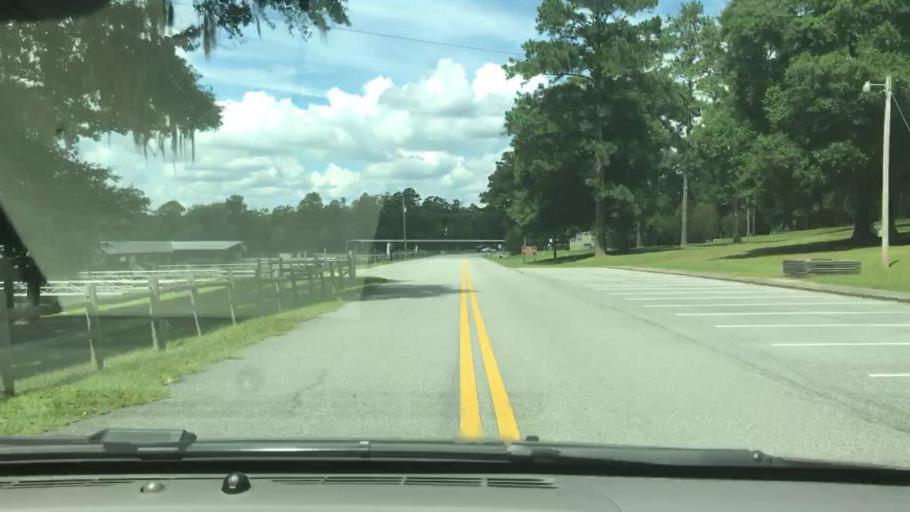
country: US
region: Georgia
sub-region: Quitman County
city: Georgetown
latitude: 32.0882
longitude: -85.0425
